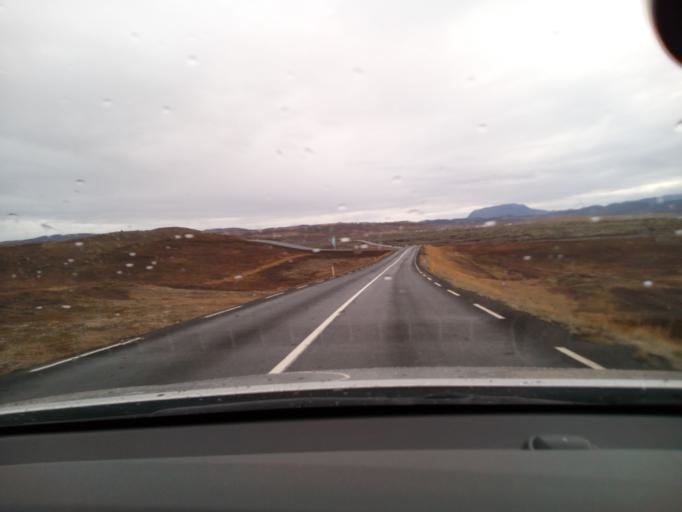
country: IS
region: Northeast
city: Laugar
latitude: 65.6593
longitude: -16.9682
